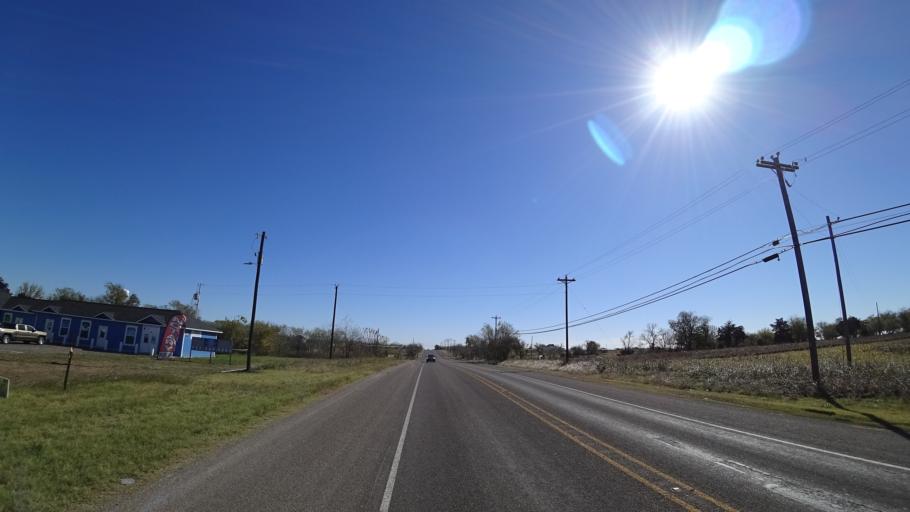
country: US
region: Texas
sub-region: Travis County
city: Garfield
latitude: 30.0996
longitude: -97.6053
